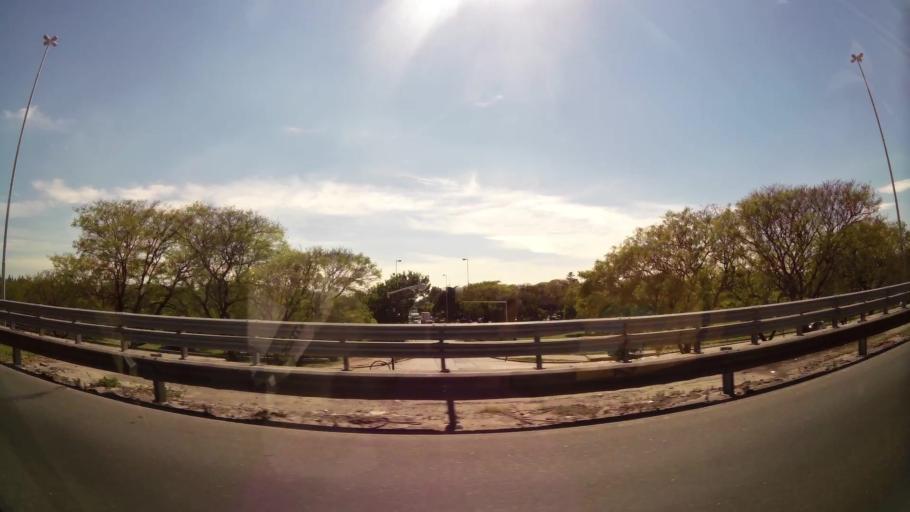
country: AR
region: Buenos Aires
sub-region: Partido de Tigre
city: Tigre
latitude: -34.4714
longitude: -58.5668
